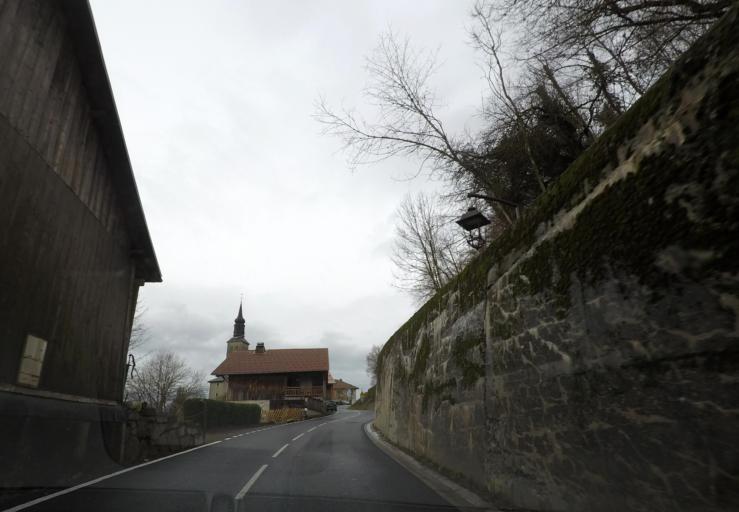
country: FR
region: Rhone-Alpes
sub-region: Departement de la Haute-Savoie
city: Araches-la-Frasse
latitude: 46.0721
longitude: 6.6157
